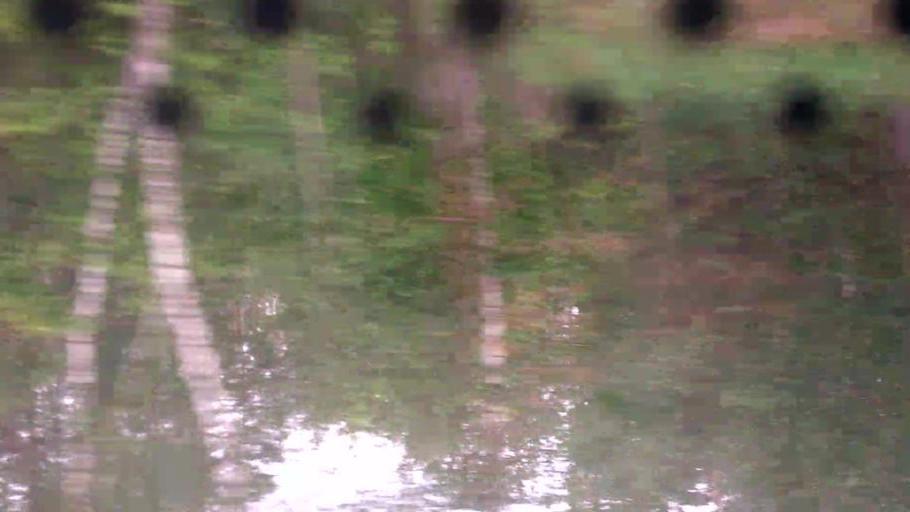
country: RU
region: Moskovskaya
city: Kolomna
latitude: 55.0524
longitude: 38.8705
